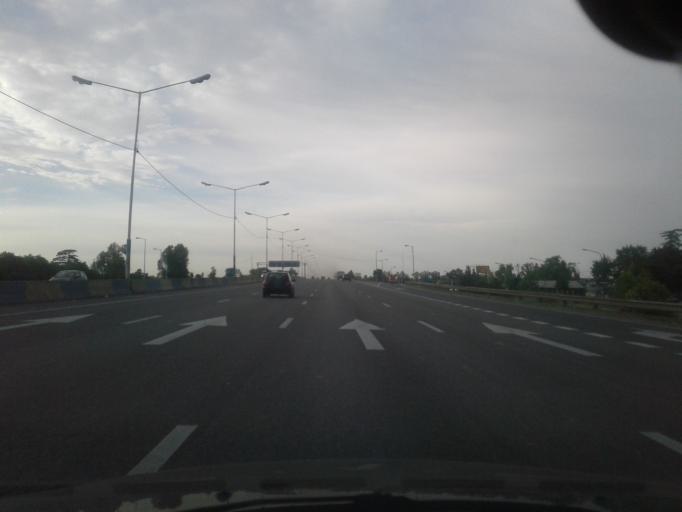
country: AR
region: Santa Fe
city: Perez
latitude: -32.9372
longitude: -60.7229
